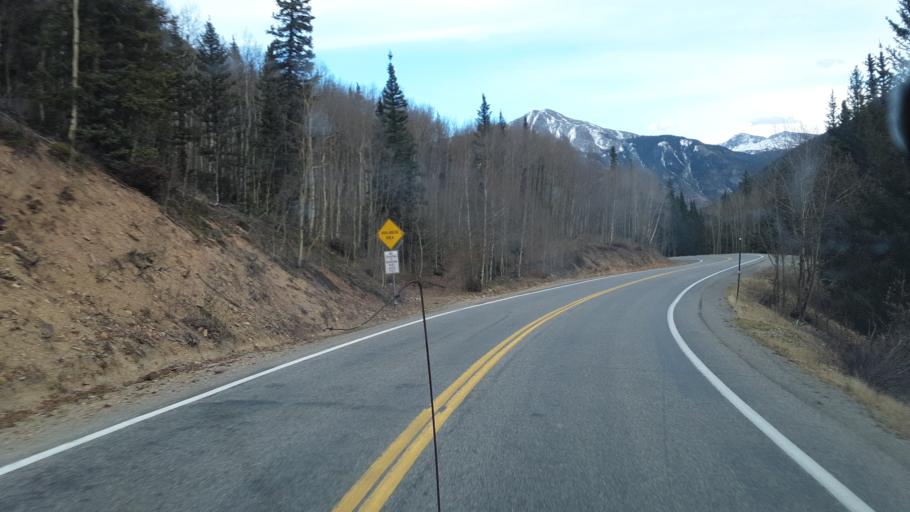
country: US
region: Colorado
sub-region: San Juan County
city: Silverton
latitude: 37.8208
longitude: -107.7090
